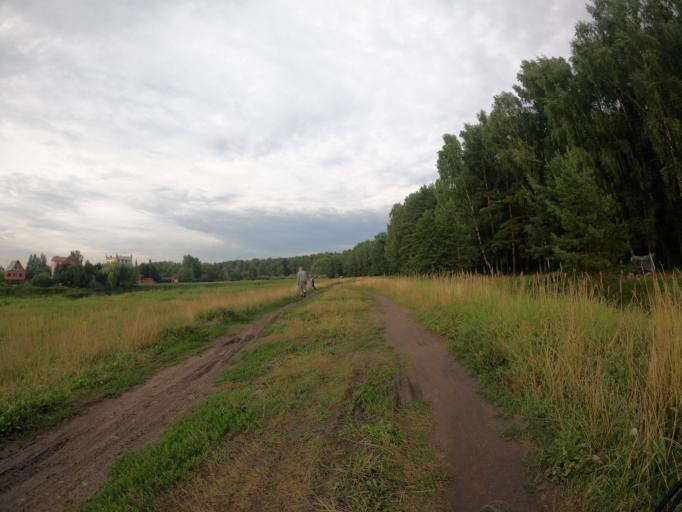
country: RU
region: Moskovskaya
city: Bykovo
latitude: 55.6512
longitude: 38.1075
